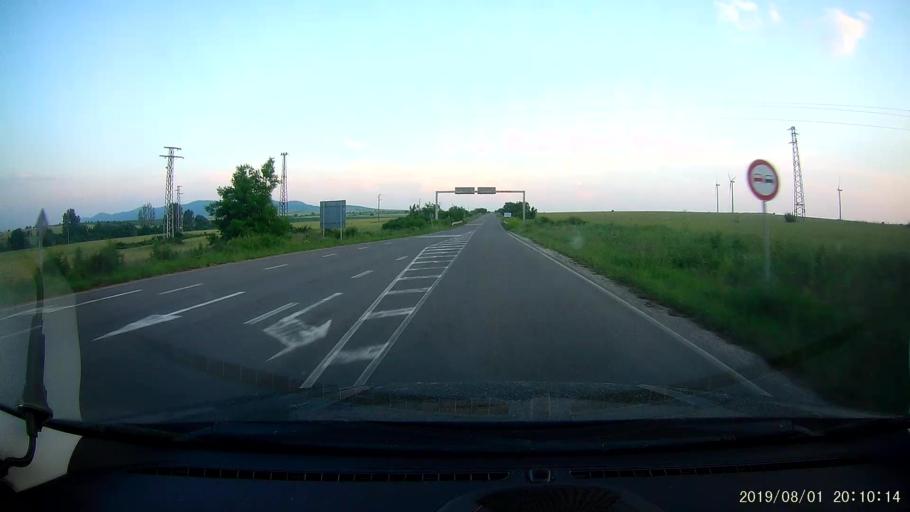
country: BG
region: Yambol
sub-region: Obshtina Yambol
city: Yambol
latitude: 42.4849
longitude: 26.5975
